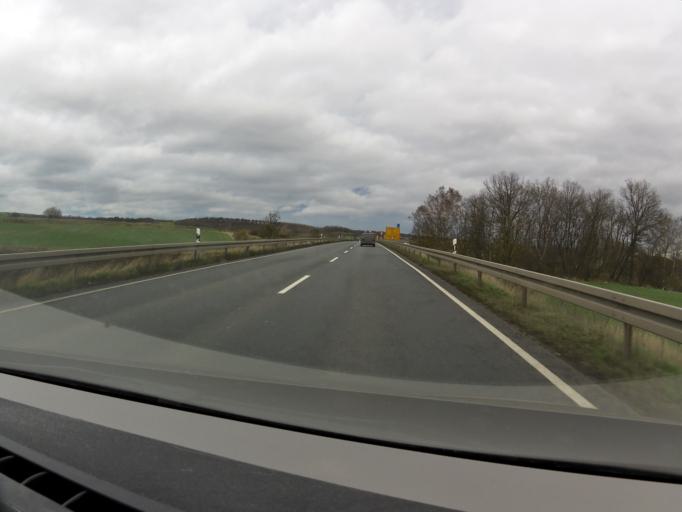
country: DE
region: Saxony-Anhalt
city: Riestedt
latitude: 51.4948
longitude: 11.3800
